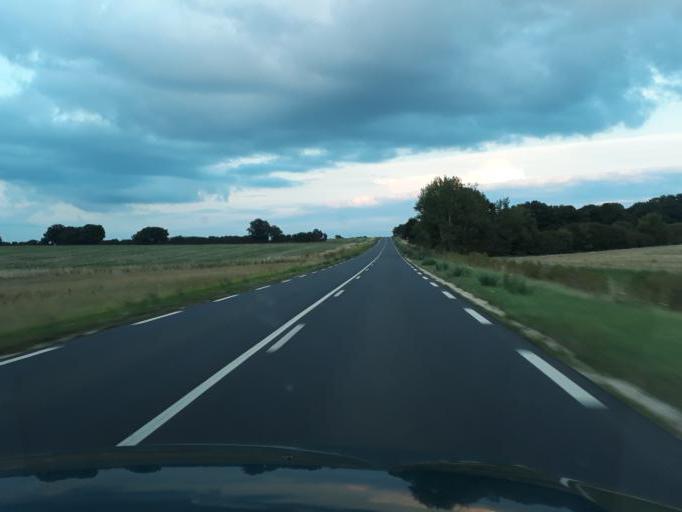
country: FR
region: Centre
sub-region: Departement du Loir-et-Cher
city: Aze
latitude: 47.8965
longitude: 0.9811
